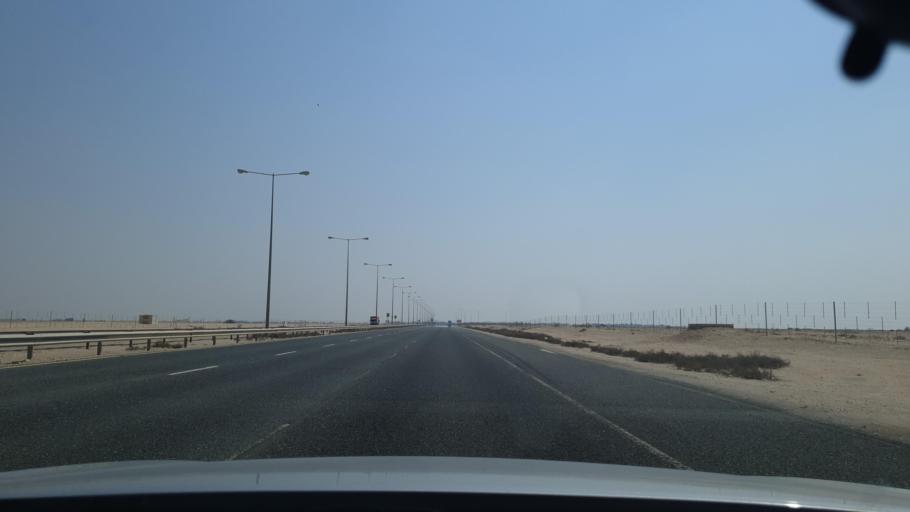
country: QA
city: Al Ghuwayriyah
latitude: 25.8020
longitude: 51.3815
